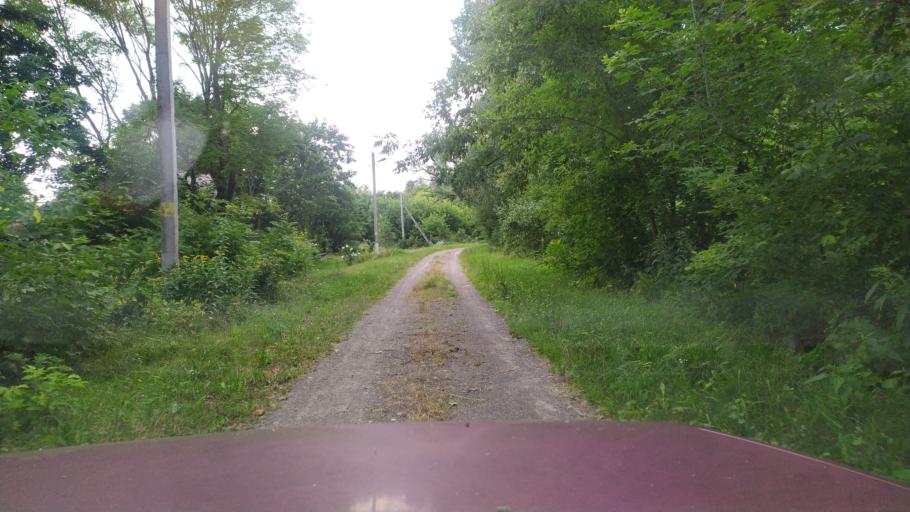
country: RU
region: Brjansk
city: Lyubovsho
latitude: 52.7470
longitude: 31.4613
